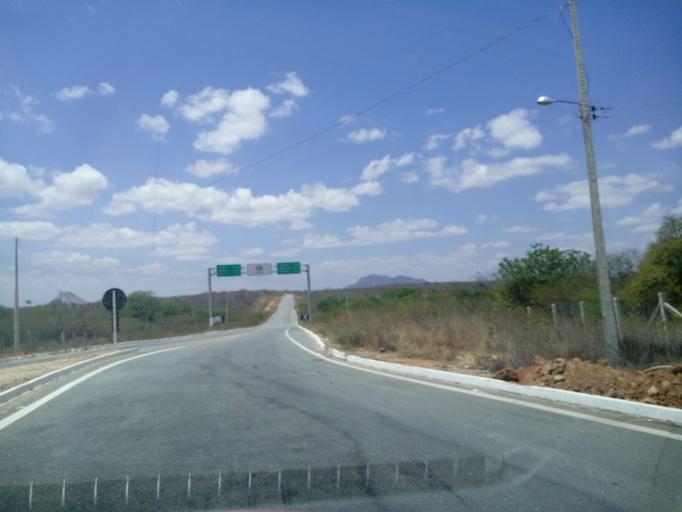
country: BR
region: Paraiba
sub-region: Patos
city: Patos
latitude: -7.0156
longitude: -37.2217
